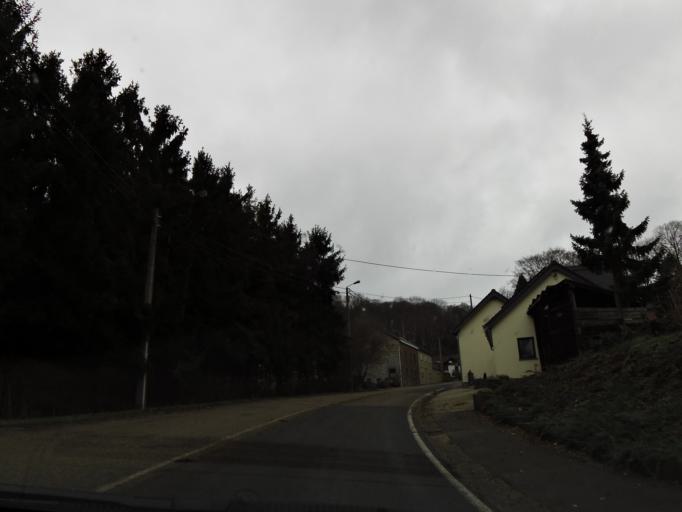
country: NL
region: Limburg
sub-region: Gemeente Vaals
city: Vaals
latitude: 50.7507
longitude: 6.0004
